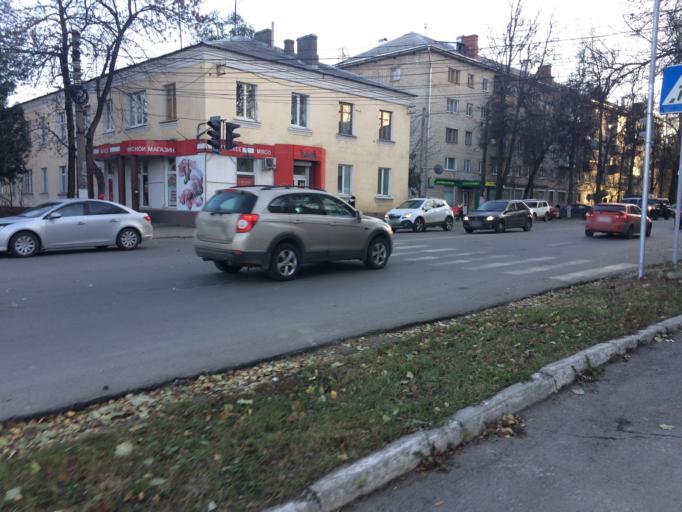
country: RU
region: Tula
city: Mendeleyevskiy
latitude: 54.1647
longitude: 37.5941
